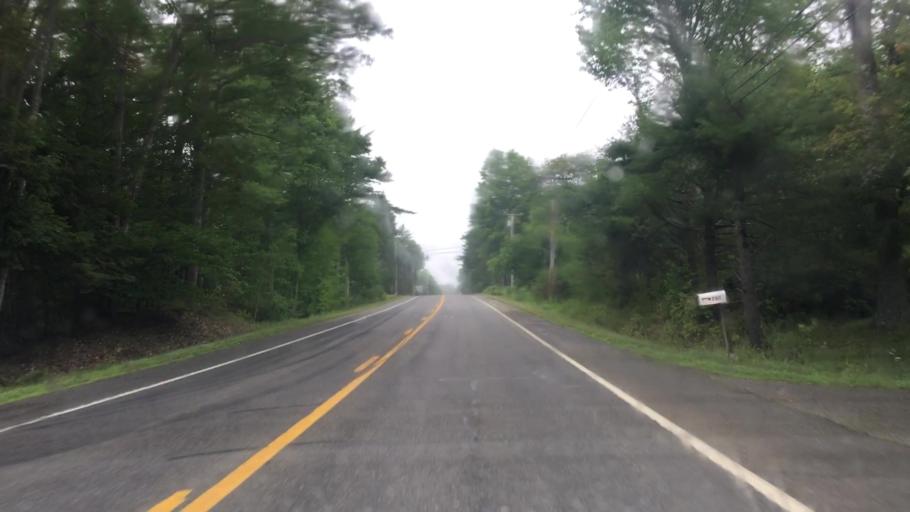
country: US
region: Maine
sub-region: Lincoln County
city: Wiscasset
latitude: 44.0568
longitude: -69.6851
